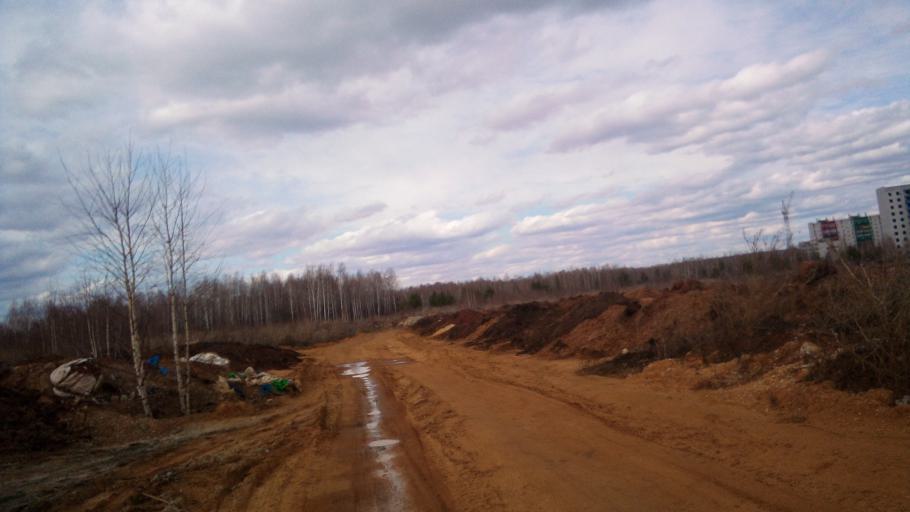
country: RU
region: Chelyabinsk
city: Sargazy
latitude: 55.1257
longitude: 61.2578
